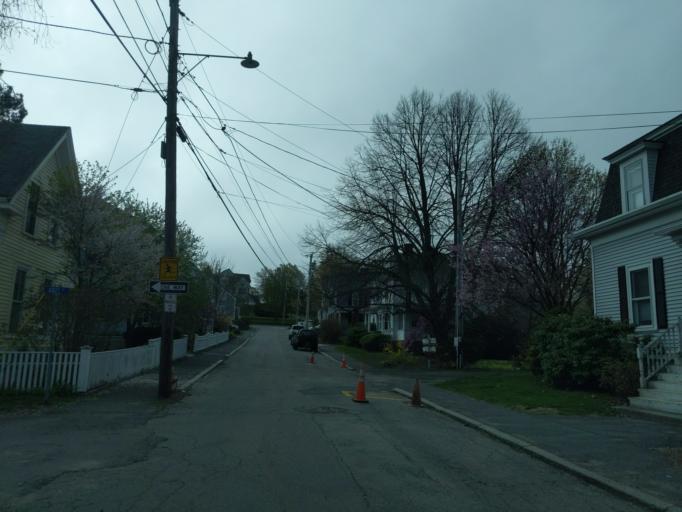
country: US
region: Massachusetts
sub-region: Essex County
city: Rockport
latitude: 42.6559
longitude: -70.6164
